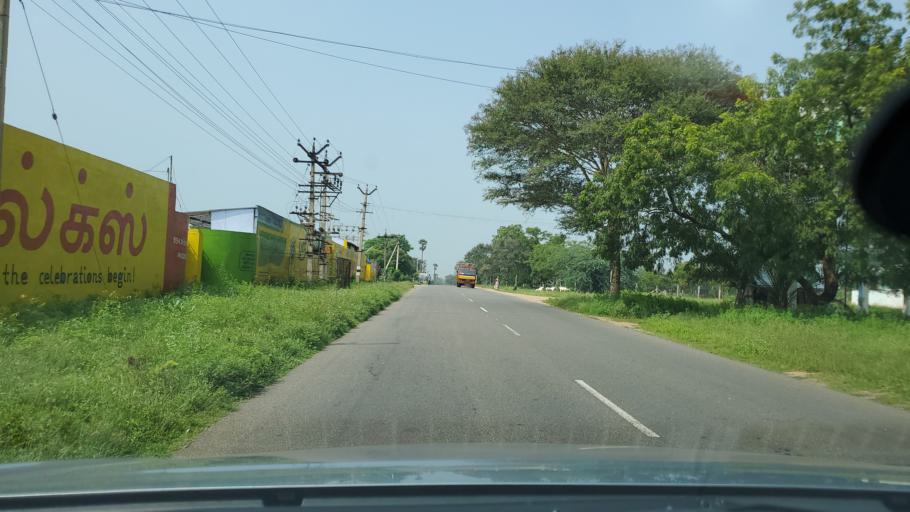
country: IN
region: Tamil Nadu
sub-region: Erode
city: Chennimalai
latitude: 11.1887
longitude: 77.6168
